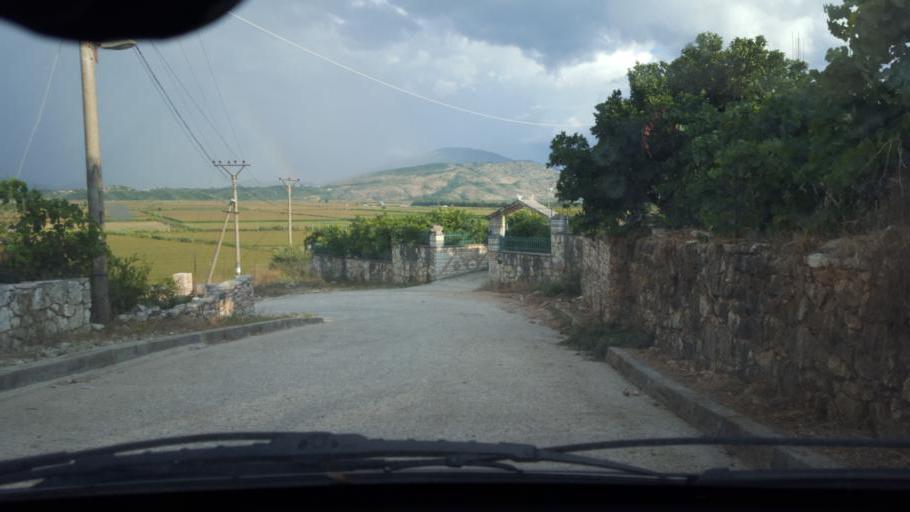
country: AL
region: Vlore
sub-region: Rrethi i Sarandes
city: Sarande
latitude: 39.8395
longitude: 20.0229
